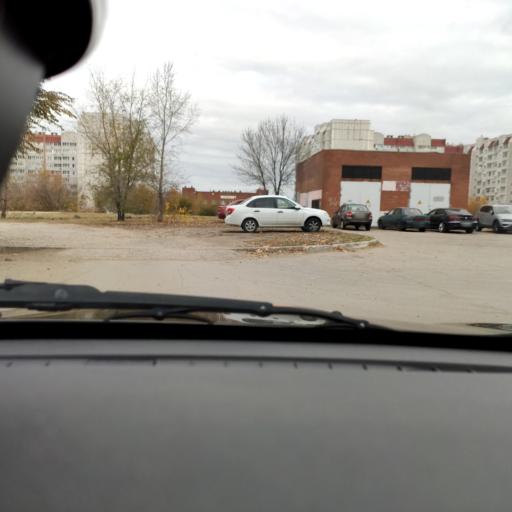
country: RU
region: Samara
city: Tol'yatti
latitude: 53.5473
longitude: 49.3220
